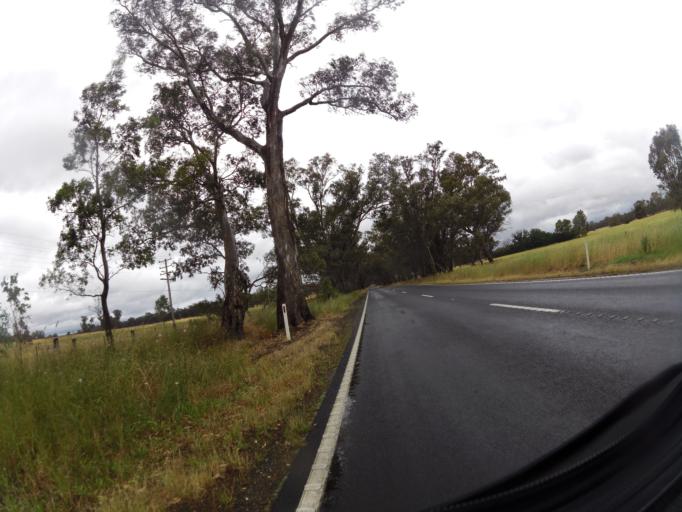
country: AU
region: Victoria
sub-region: Mount Alexander
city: Castlemaine
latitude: -37.0953
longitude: 144.1292
